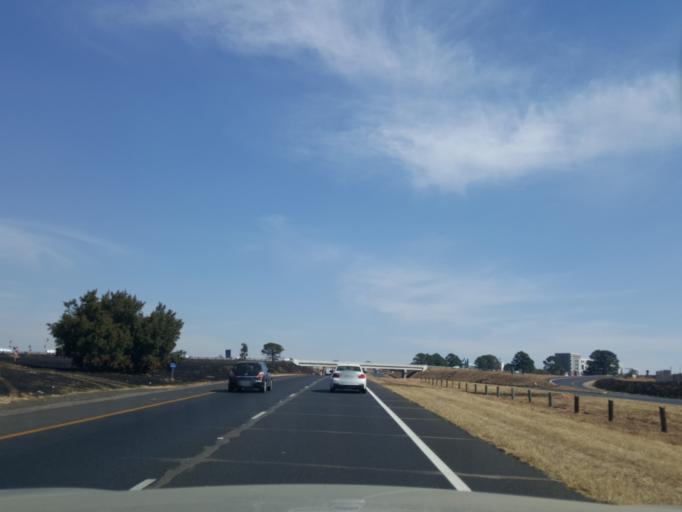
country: ZA
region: Mpumalanga
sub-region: Nkangala District Municipality
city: Witbank
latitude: -25.8857
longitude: 29.2751
